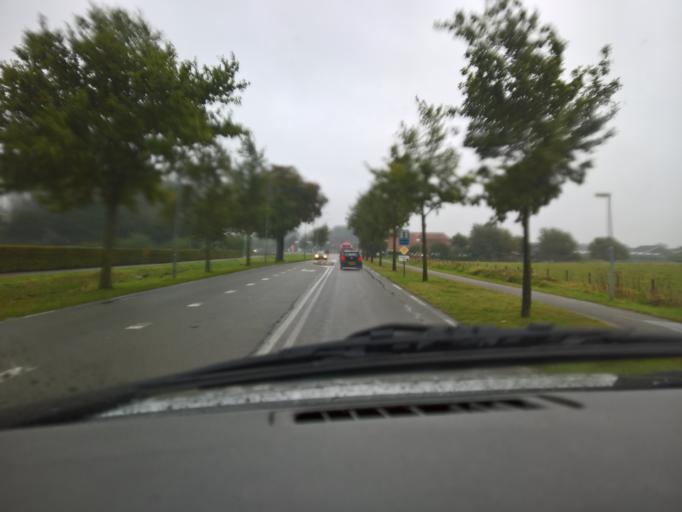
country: NL
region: Gelderland
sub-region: Gemeente Nijmegen
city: Lindenholt
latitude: 51.8592
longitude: 5.8001
